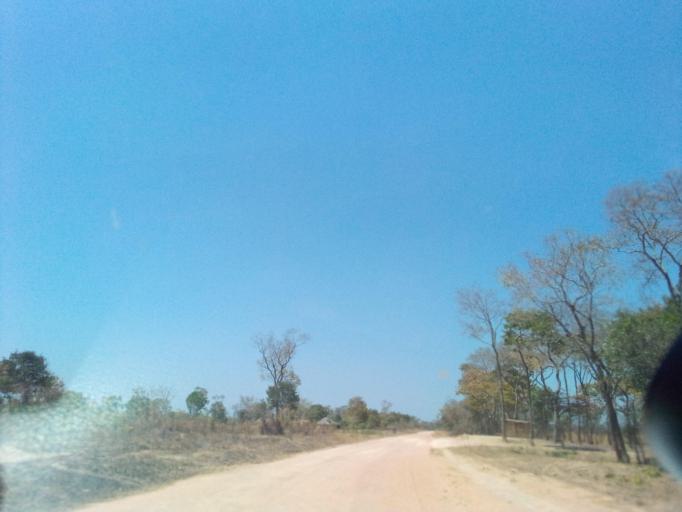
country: ZM
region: Northern
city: Mpika
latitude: -12.2275
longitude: 30.6563
